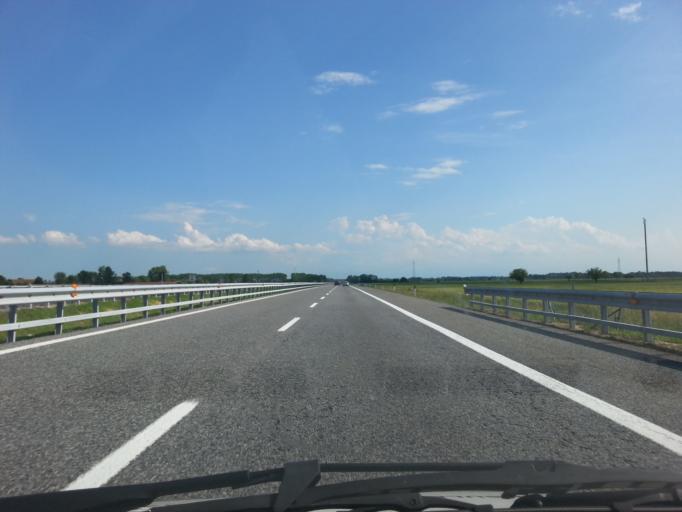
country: IT
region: Piedmont
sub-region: Provincia di Cuneo
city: Sommariva del Bosco
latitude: 44.7327
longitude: 7.7548
